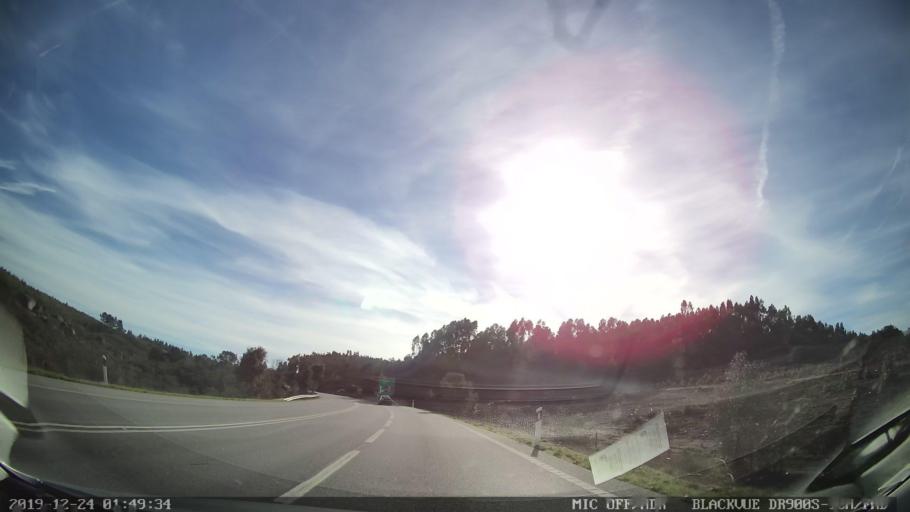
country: PT
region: Portalegre
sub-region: Nisa
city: Nisa
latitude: 39.5064
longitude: -7.7714
